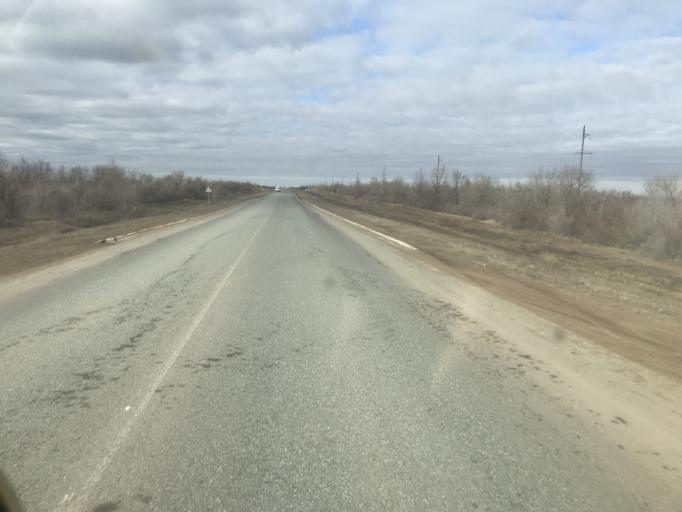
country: KZ
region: Batys Qazaqstan
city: Krugloozernoe
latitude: 51.1925
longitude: 51.0884
